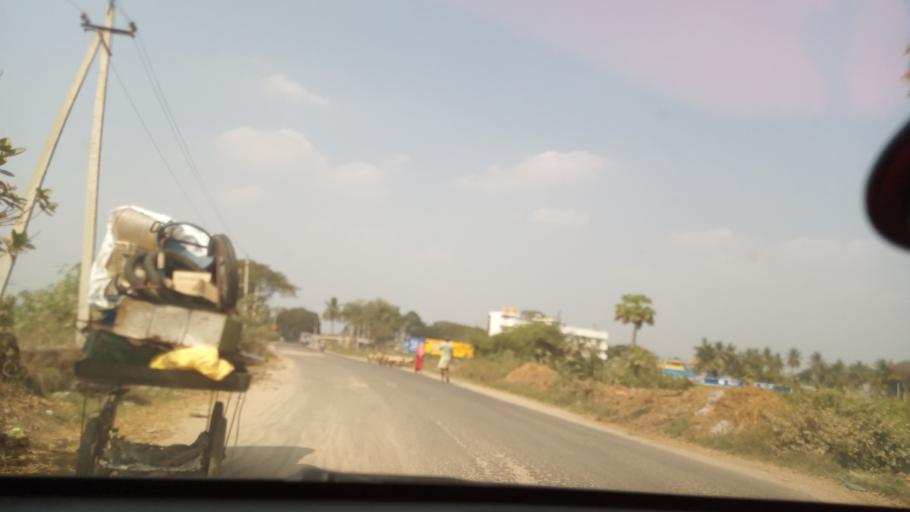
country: IN
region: Karnataka
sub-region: Mysore
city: Nanjangud
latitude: 12.1160
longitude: 76.7021
